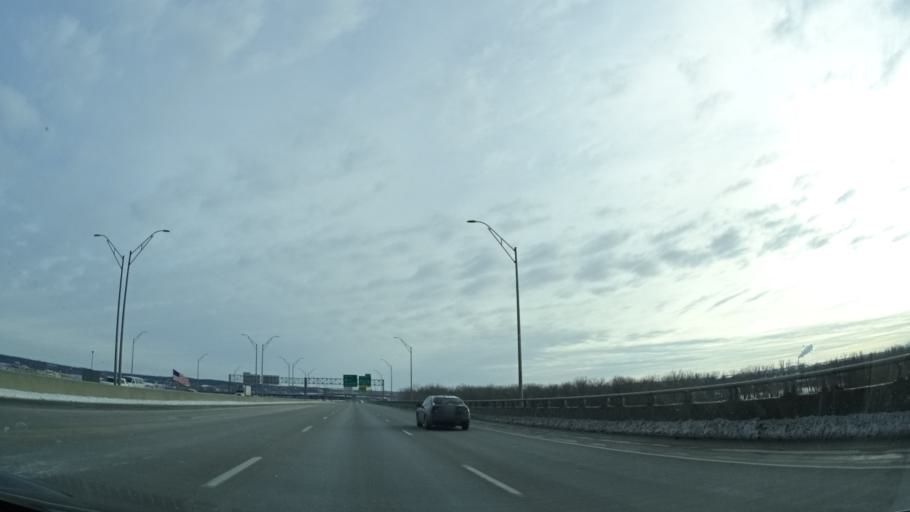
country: US
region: Nebraska
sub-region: Douglas County
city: Omaha
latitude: 41.2314
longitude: -95.9139
